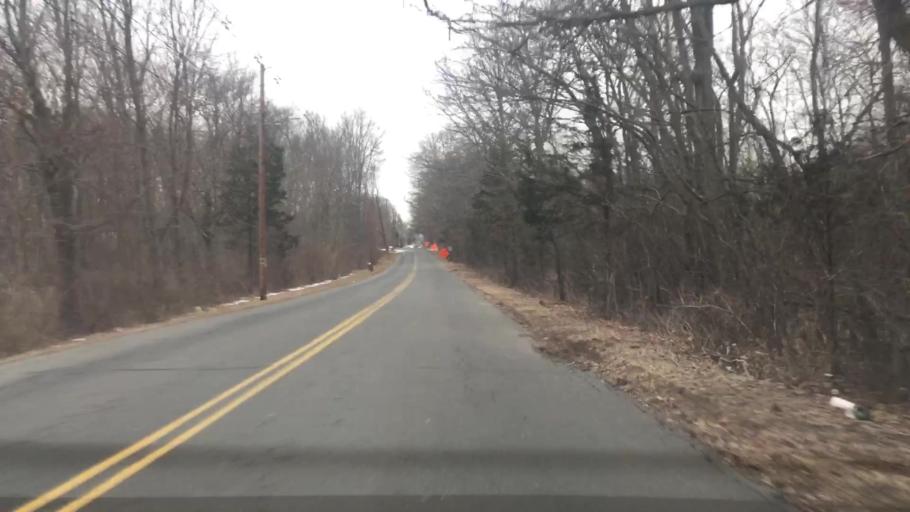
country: US
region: Connecticut
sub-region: Hartford County
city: Kensington
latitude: 41.6189
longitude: -72.7659
